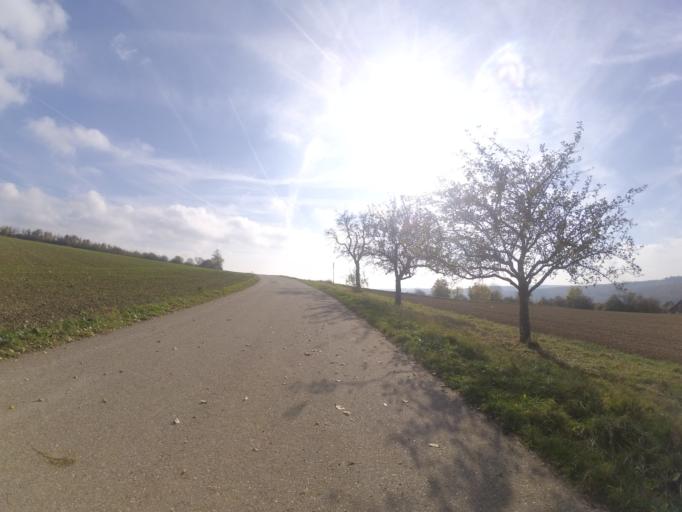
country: DE
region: Baden-Wuerttemberg
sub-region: Tuebingen Region
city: Dornstadt
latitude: 48.4182
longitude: 9.9298
